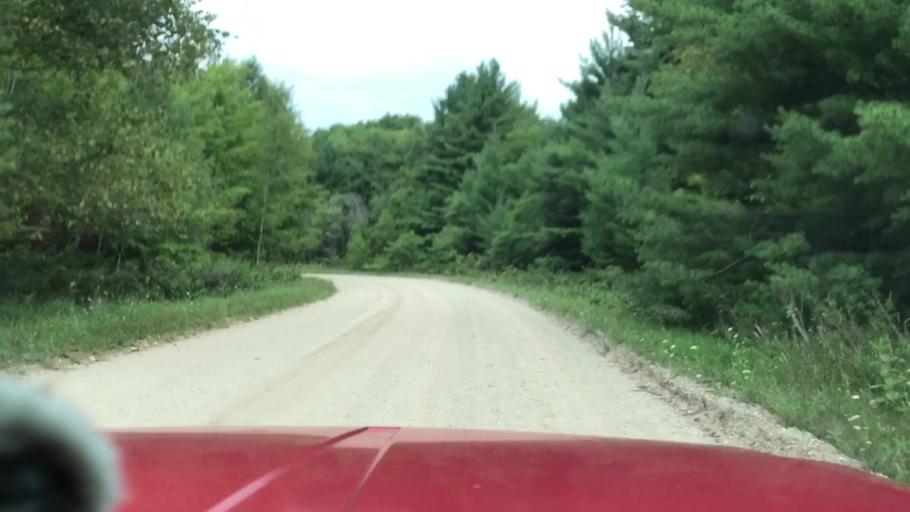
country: US
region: Michigan
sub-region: Charlevoix County
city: Charlevoix
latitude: 45.7212
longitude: -85.5621
